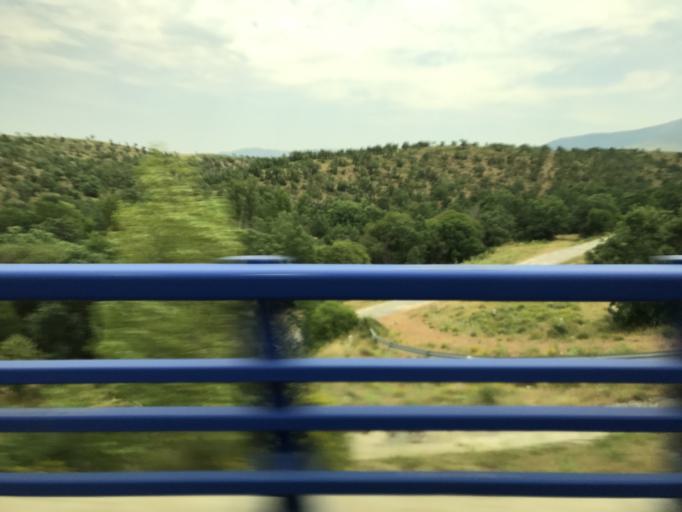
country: ES
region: Castille and Leon
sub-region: Provincia de Segovia
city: Cerezo de Abajo
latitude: 41.2145
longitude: -3.5809
